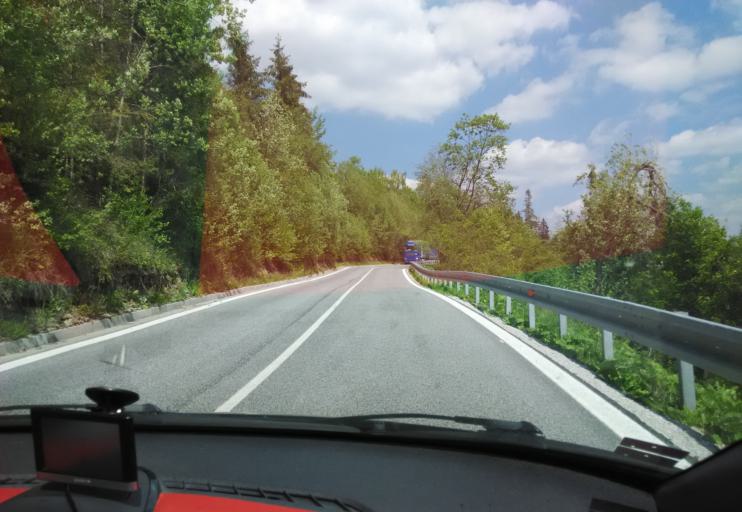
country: SK
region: Kosicky
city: Dobsina
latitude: 48.8451
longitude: 20.4394
